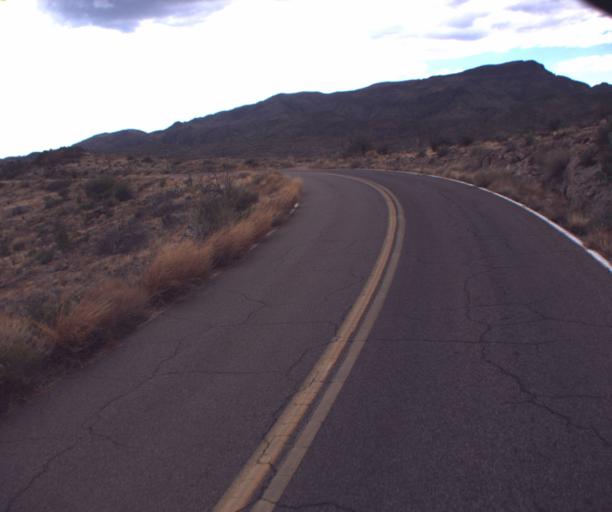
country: US
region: Arizona
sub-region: Pinal County
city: Gold Camp
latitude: 33.5402
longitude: -111.3278
